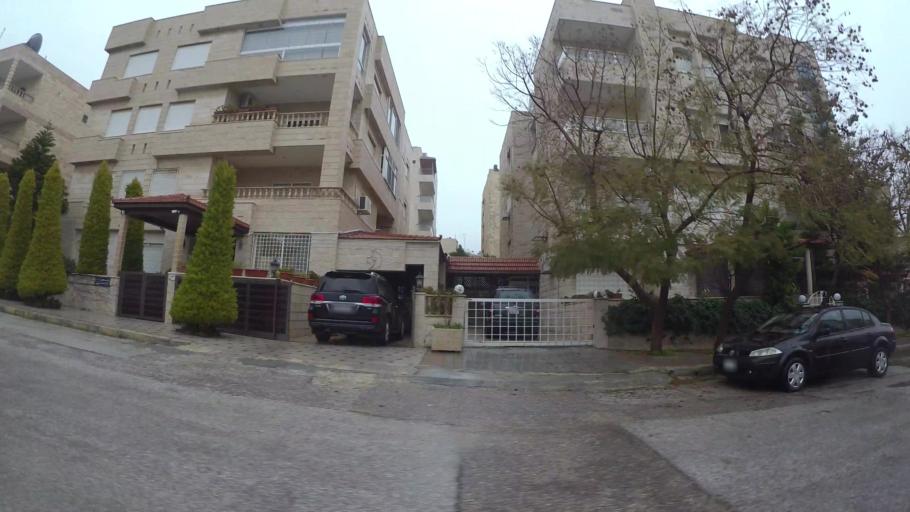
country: JO
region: Amman
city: Wadi as Sir
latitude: 31.9718
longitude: 35.8658
